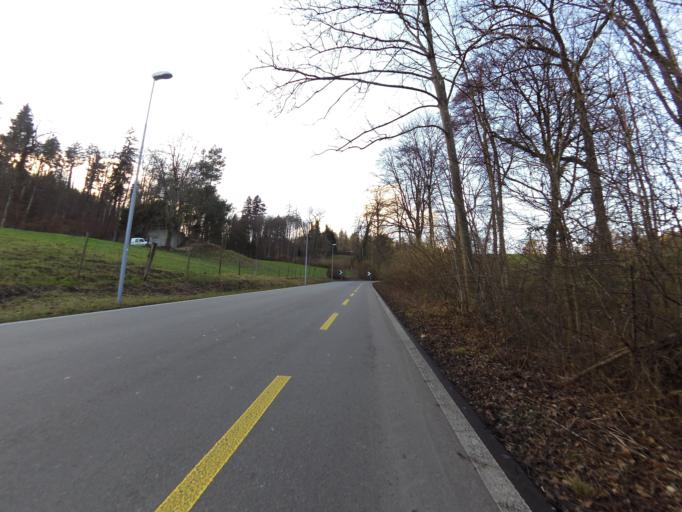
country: CH
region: Zurich
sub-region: Bezirk Zuerich
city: Zuerich (Kreis 9)
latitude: 47.3728
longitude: 8.4770
